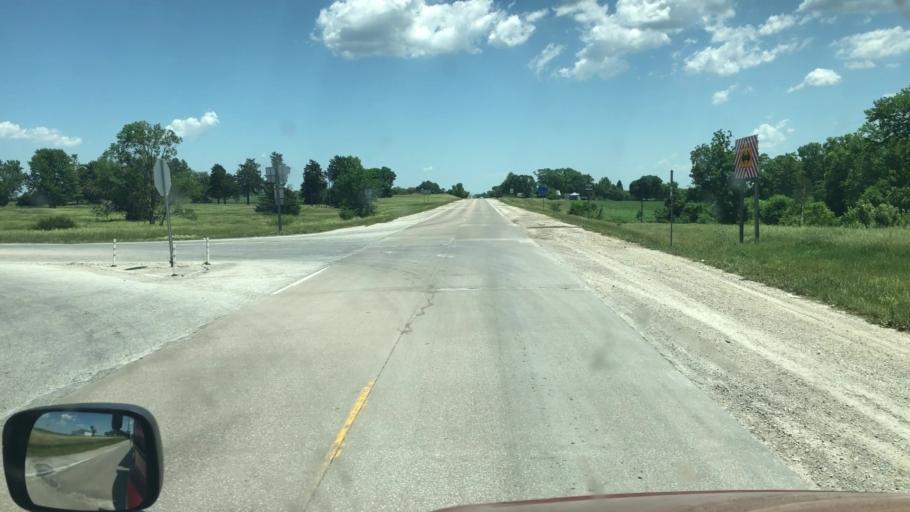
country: US
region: Missouri
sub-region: Marion County
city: Palmyra
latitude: 39.6925
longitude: -91.5048
